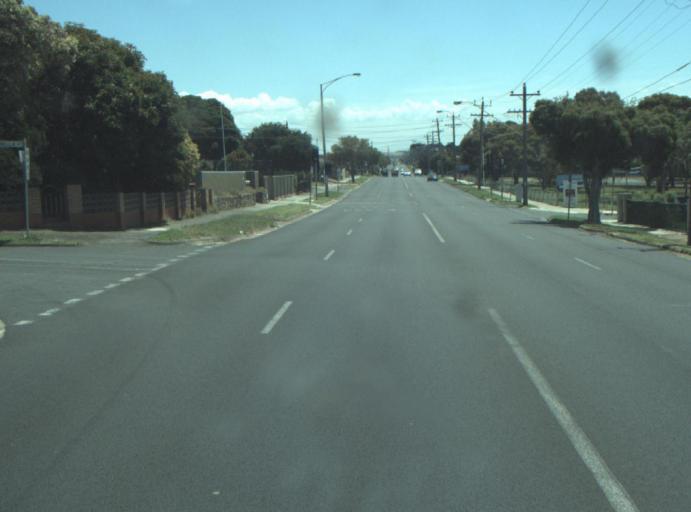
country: AU
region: Victoria
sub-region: Greater Geelong
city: Bell Park
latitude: -38.1064
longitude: 144.3324
